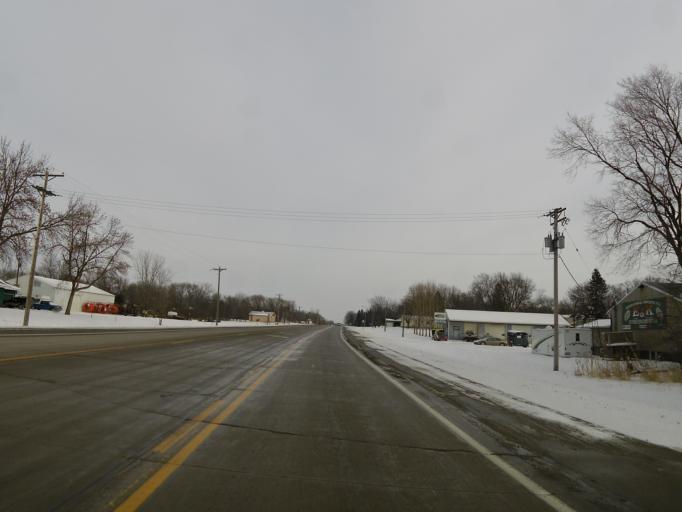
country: US
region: Minnesota
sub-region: McLeod County
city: Glencoe
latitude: 44.9061
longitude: -94.2034
